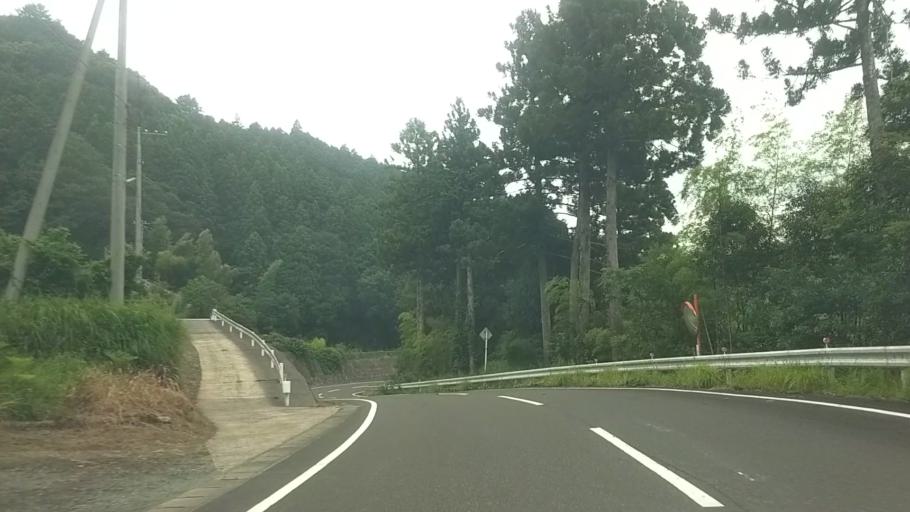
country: JP
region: Chiba
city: Kawaguchi
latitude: 35.1859
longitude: 140.1353
